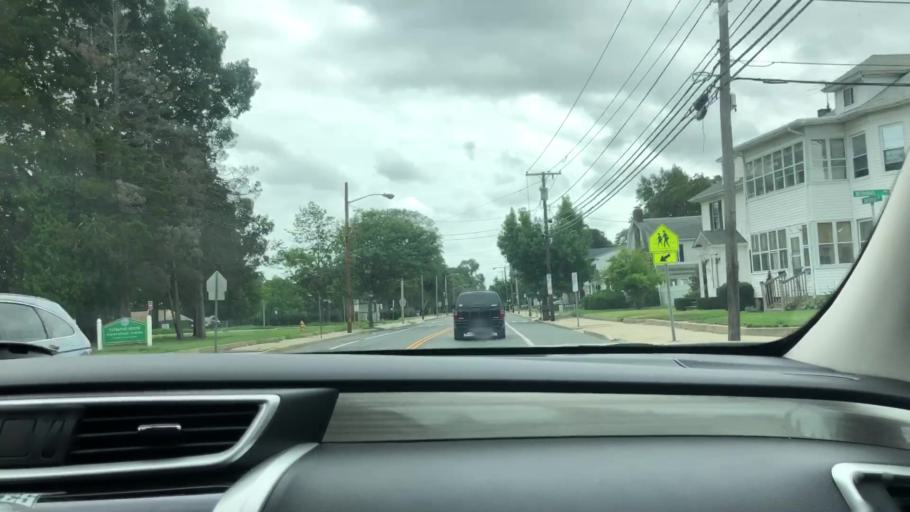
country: US
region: Rhode Island
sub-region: Providence County
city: Central Falls
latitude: 41.8680
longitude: -71.4131
